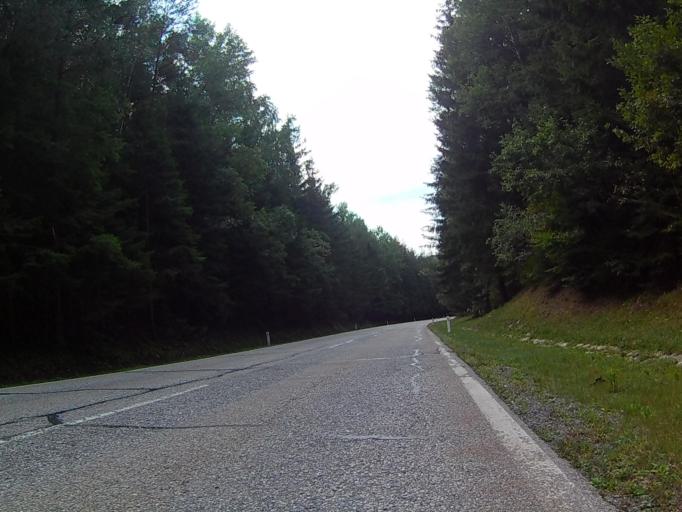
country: AT
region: Styria
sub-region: Politischer Bezirk Deutschlandsberg
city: Soboth
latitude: 46.6833
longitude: 15.0917
